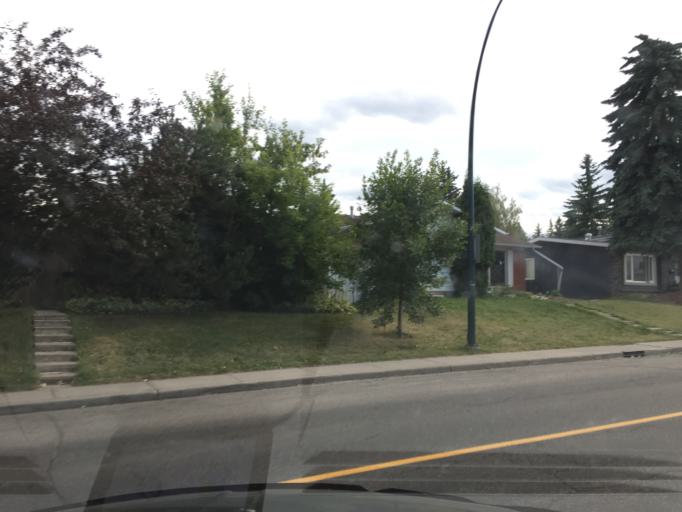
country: CA
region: Alberta
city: Calgary
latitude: 50.9479
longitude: -114.0827
